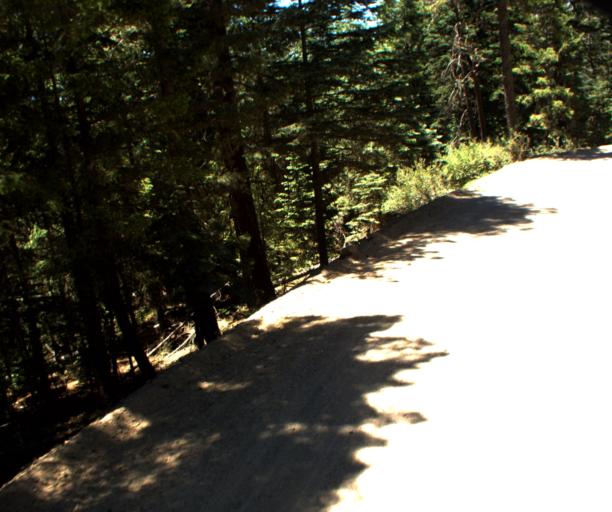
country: US
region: Arizona
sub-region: Graham County
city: Swift Trail Junction
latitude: 32.6700
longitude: -109.8820
